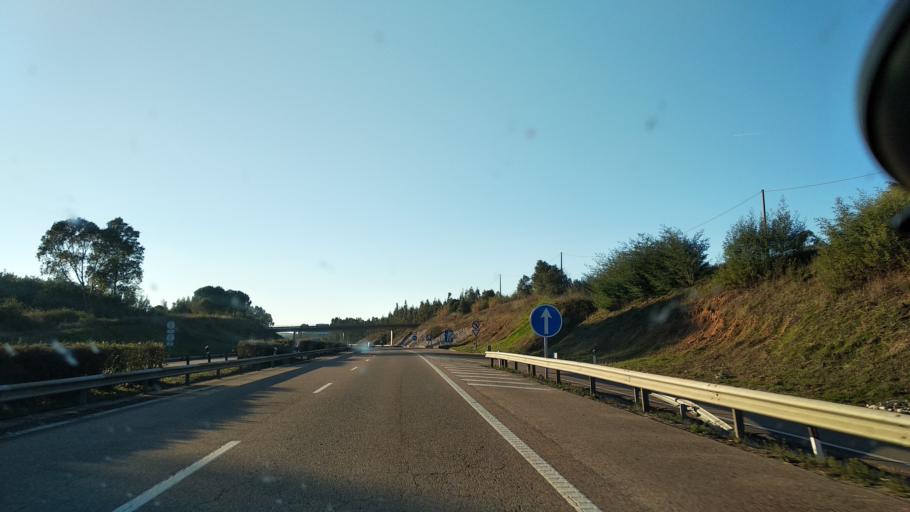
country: PT
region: Santarem
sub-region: Chamusca
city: Vila Nova da Barquinha
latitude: 39.4872
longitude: -8.3918
